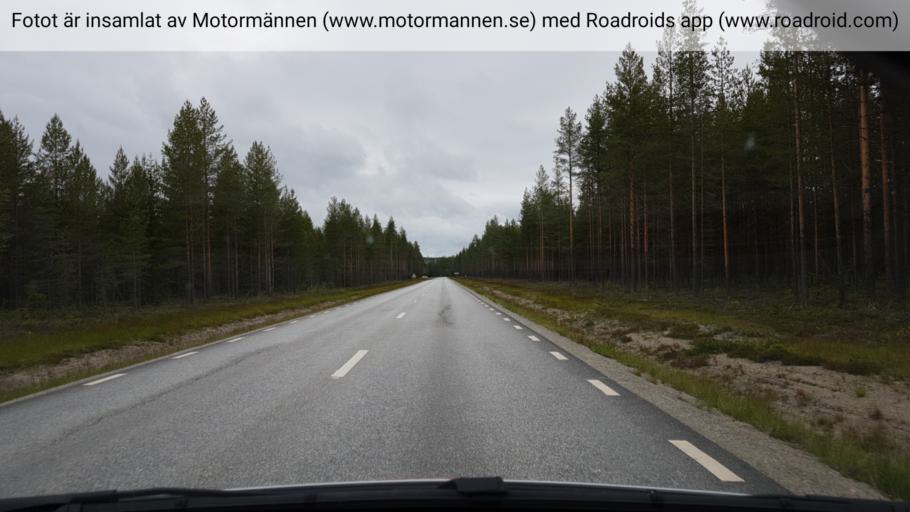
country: SE
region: Vaesterbotten
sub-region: Vindelns Kommun
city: Vindeln
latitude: 64.0969
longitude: 19.6067
